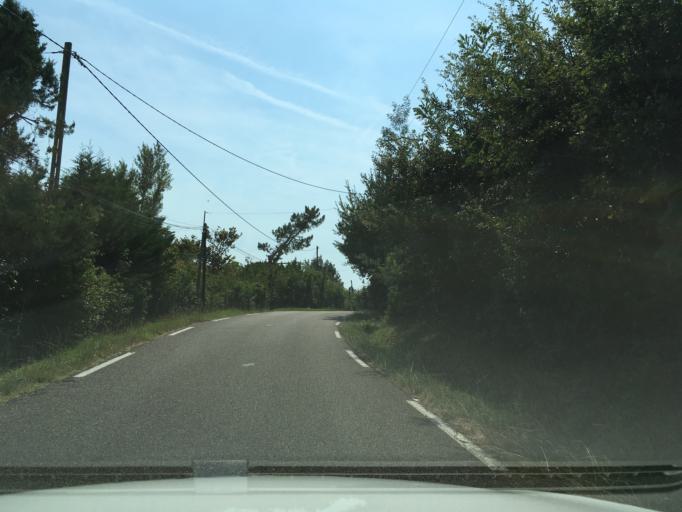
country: FR
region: Midi-Pyrenees
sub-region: Departement du Tarn-et-Garonne
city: Corbarieu
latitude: 43.9756
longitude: 1.3782
